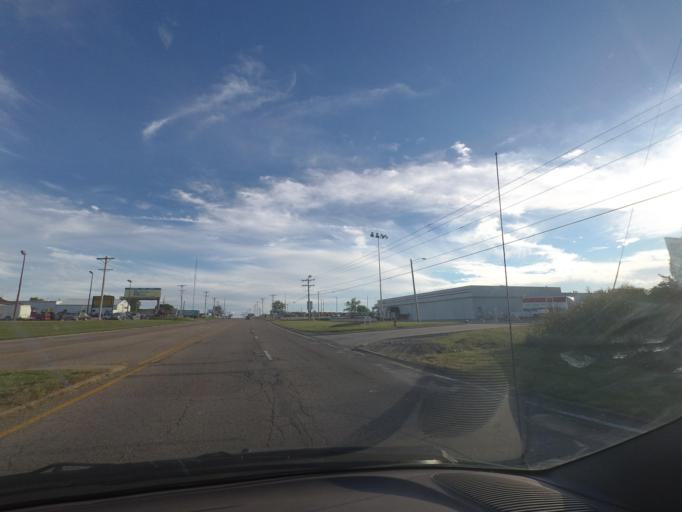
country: US
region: Illinois
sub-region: Sangamon County
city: Grandview
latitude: 39.7981
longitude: -89.6059
